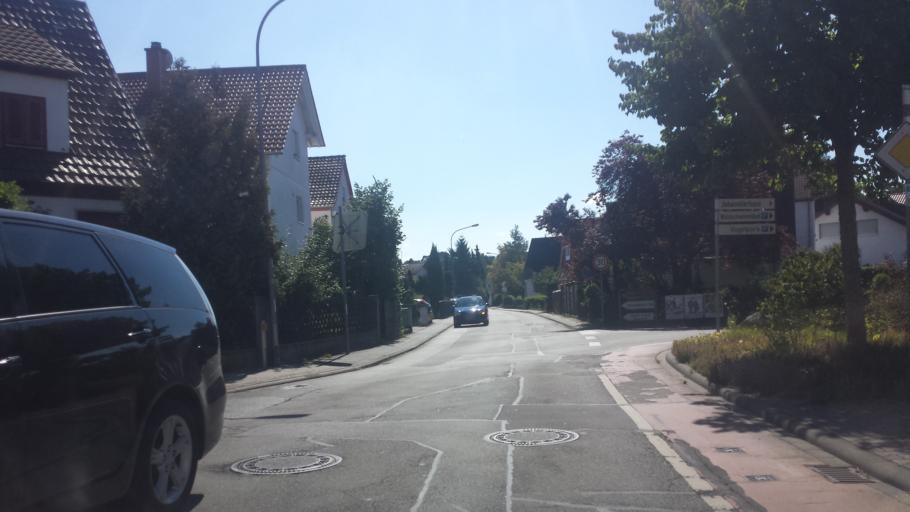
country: DE
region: Hesse
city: Lorsch
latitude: 49.6477
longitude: 8.5595
